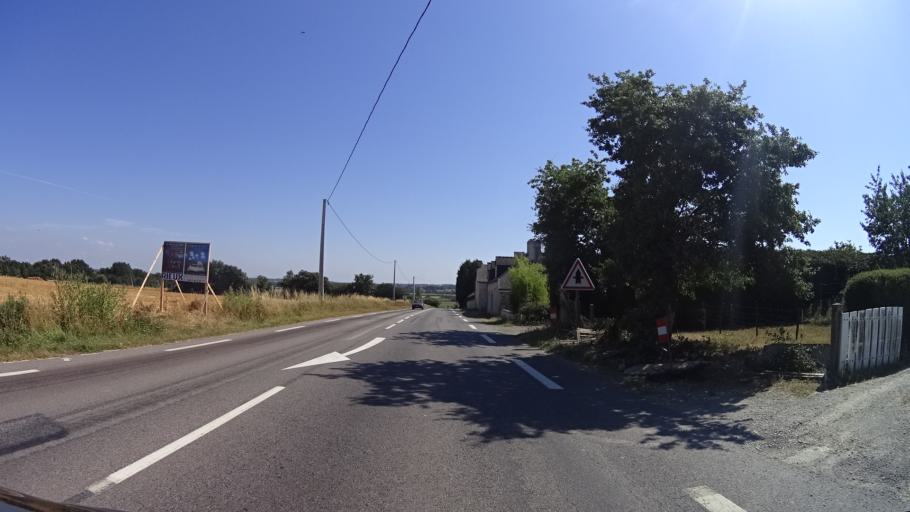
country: FR
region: Brittany
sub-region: Departement du Morbihan
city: Rieux
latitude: 47.5882
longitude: -2.1102
